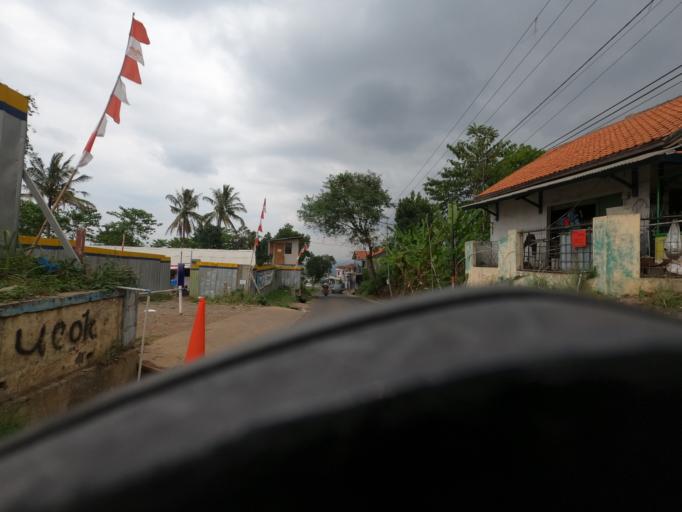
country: ID
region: West Java
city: Padalarang
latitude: -6.8358
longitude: 107.5141
